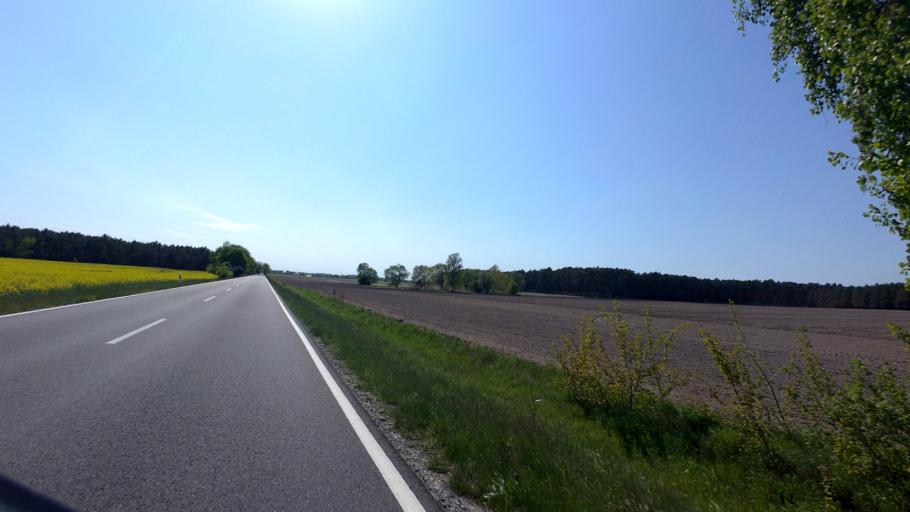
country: DE
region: Brandenburg
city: Neu Zauche
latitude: 52.0390
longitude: 14.1063
